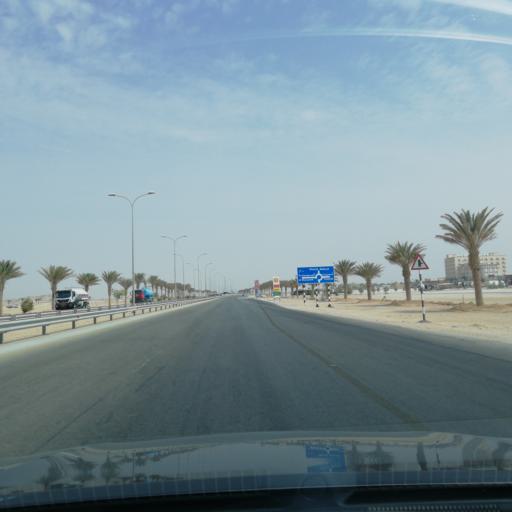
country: OM
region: Zufar
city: Salalah
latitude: 17.6077
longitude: 54.0342
